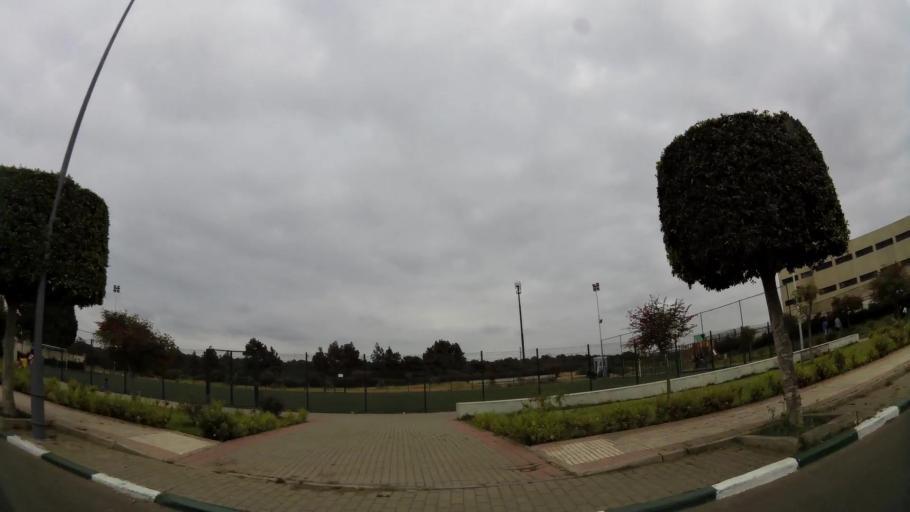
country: MA
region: Rabat-Sale-Zemmour-Zaer
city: Sale
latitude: 34.0309
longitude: -6.7967
